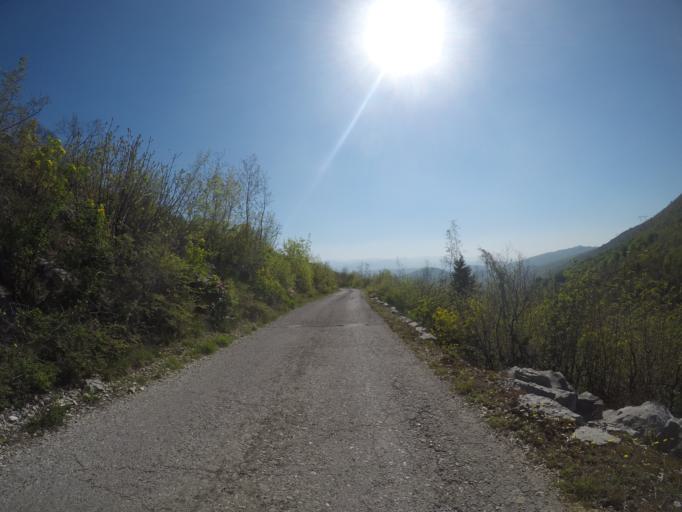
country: ME
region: Danilovgrad
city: Danilovgrad
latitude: 42.5141
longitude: 19.0654
